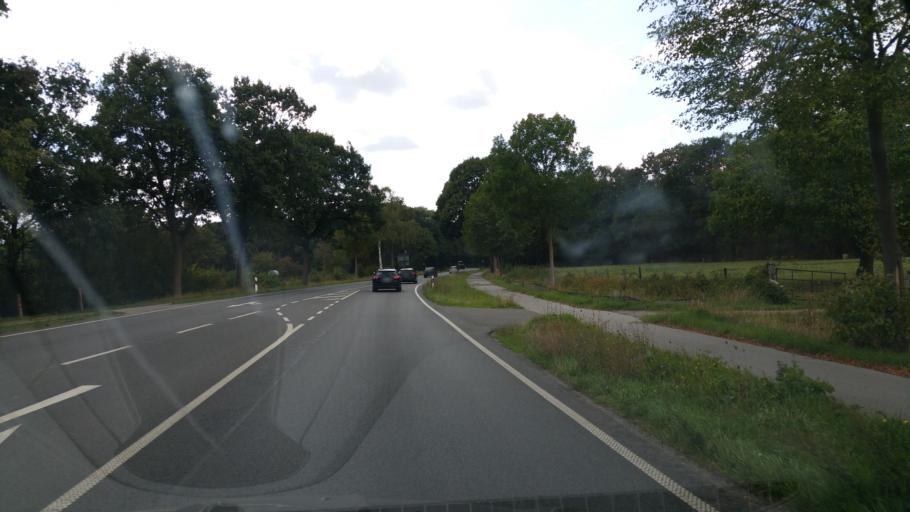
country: DE
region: North Rhine-Westphalia
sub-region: Regierungsbezirk Dusseldorf
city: Hamminkeln
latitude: 51.7286
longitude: 6.5998
